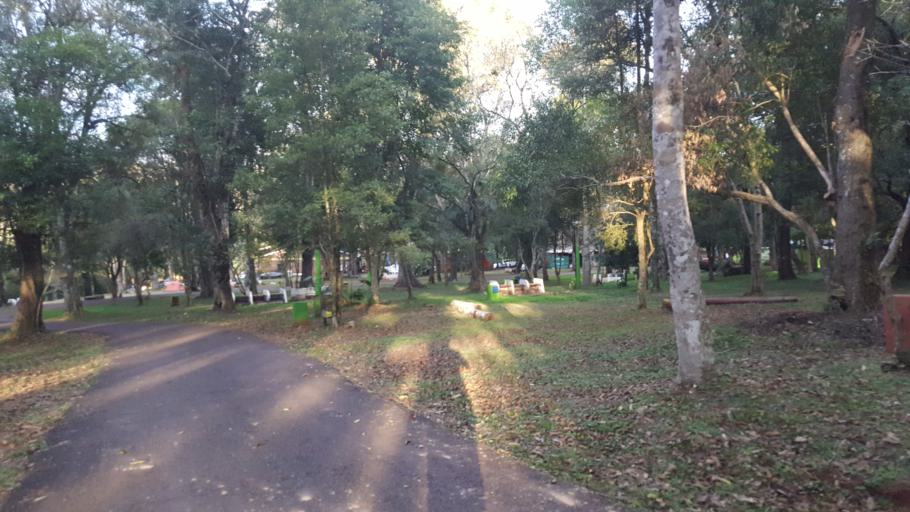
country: AR
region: Misiones
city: Puerto Leoni
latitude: -26.9990
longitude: -55.1798
